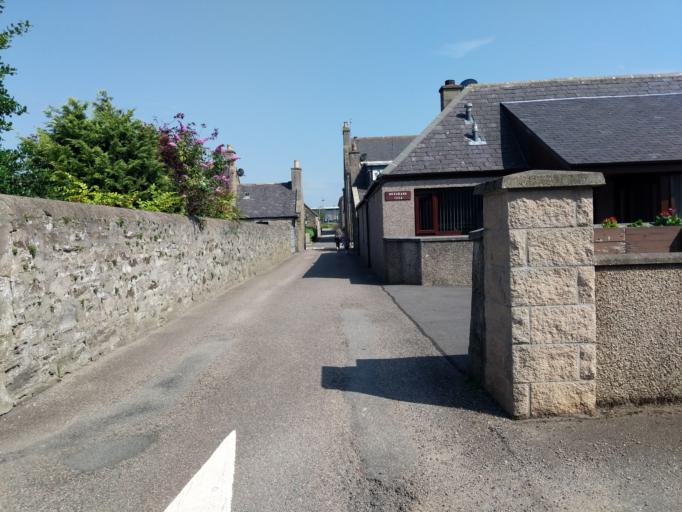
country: GB
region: Scotland
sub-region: Moray
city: Keith
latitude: 57.5417
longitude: -2.9489
